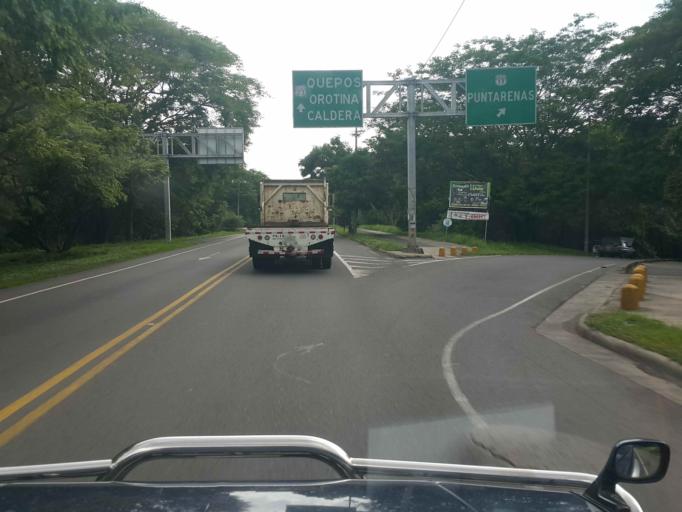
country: CR
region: Puntarenas
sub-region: Canton Central de Puntarenas
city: Chacarita
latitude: 9.9779
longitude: -84.7398
